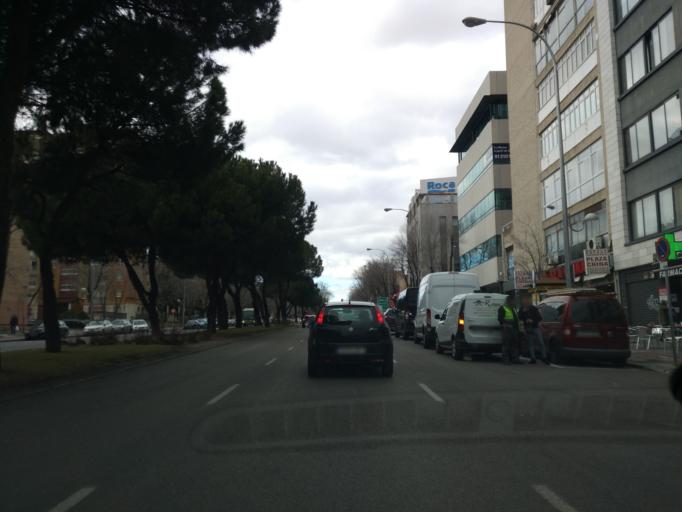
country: ES
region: Madrid
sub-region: Provincia de Madrid
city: San Blas
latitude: 40.4317
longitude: -3.6333
